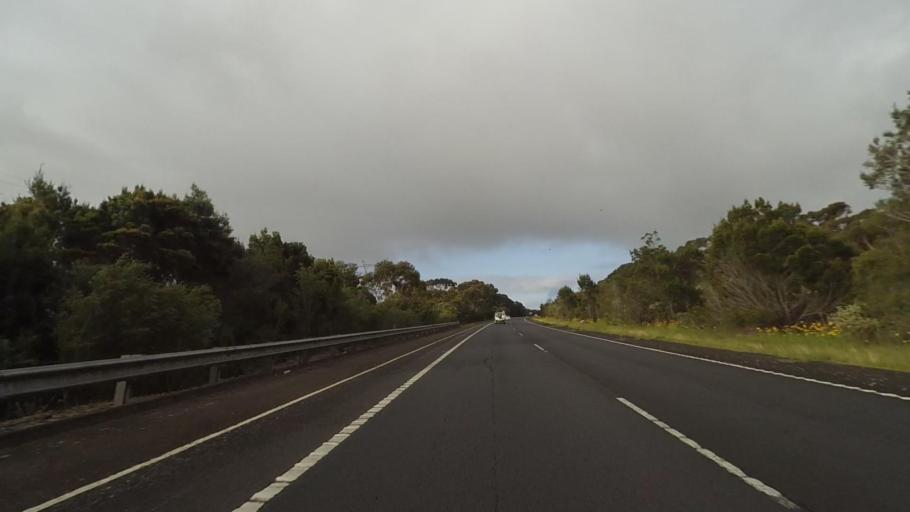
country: AU
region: New South Wales
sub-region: Wollongong
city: Bulli
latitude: -34.2493
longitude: 150.9355
